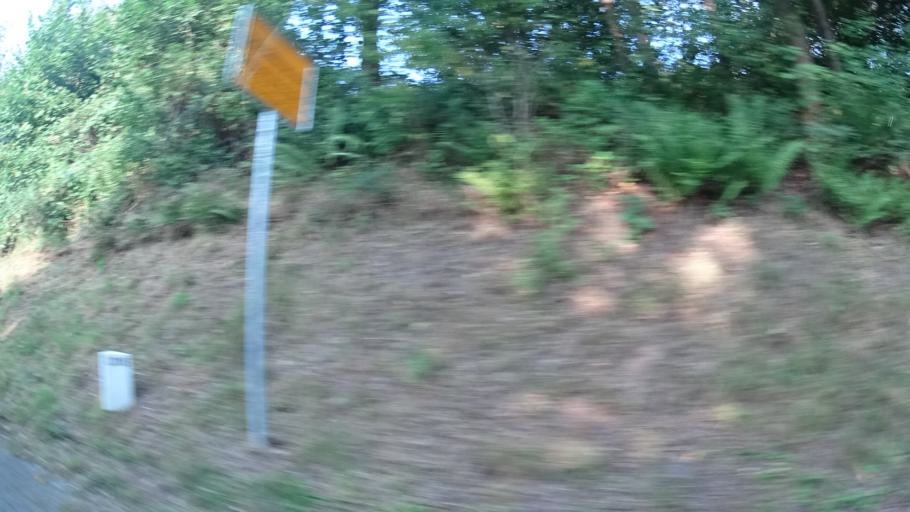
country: DE
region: Baden-Wuerttemberg
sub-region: Karlsruhe Region
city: Heddesbach
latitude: 49.5222
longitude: 8.8621
